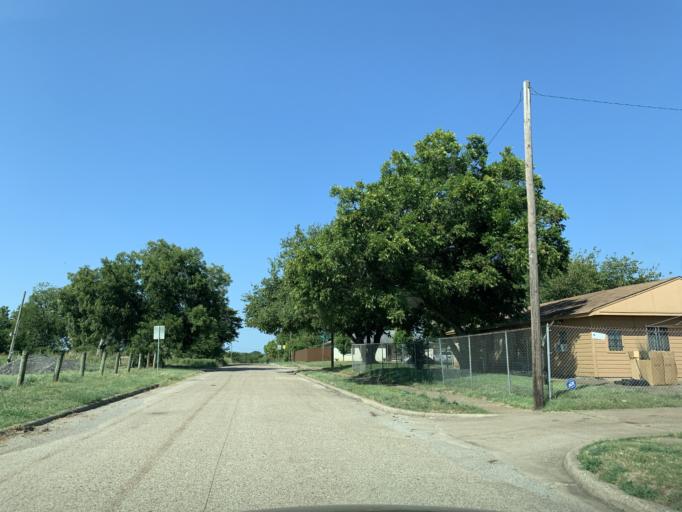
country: US
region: Texas
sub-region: Dallas County
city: Hutchins
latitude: 32.6660
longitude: -96.7460
